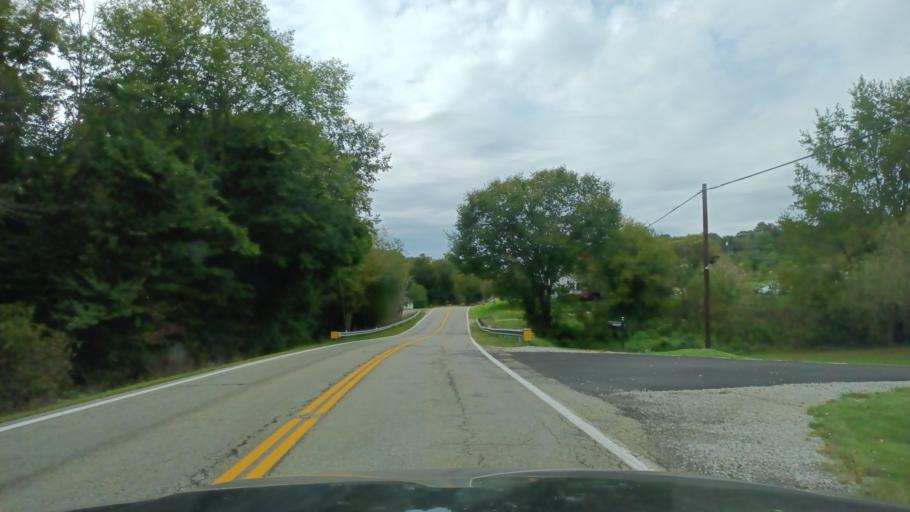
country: US
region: Ohio
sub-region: Vinton County
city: McArthur
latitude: 39.2720
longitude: -82.5205
